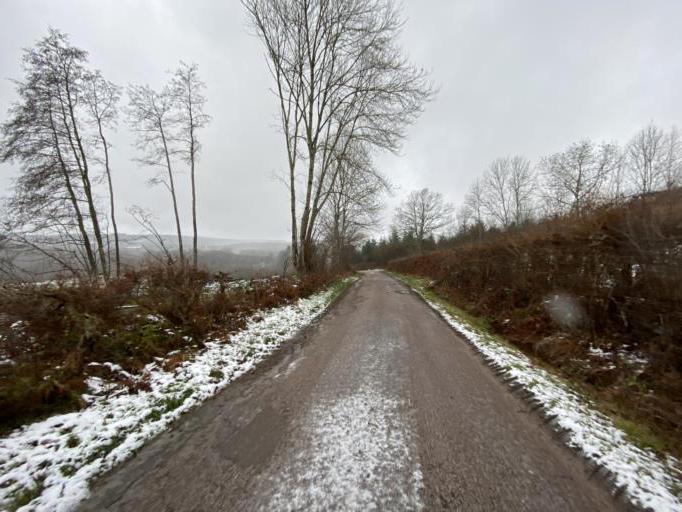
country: FR
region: Bourgogne
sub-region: Departement de la Cote-d'Or
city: Saulieu
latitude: 47.2672
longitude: 4.1590
